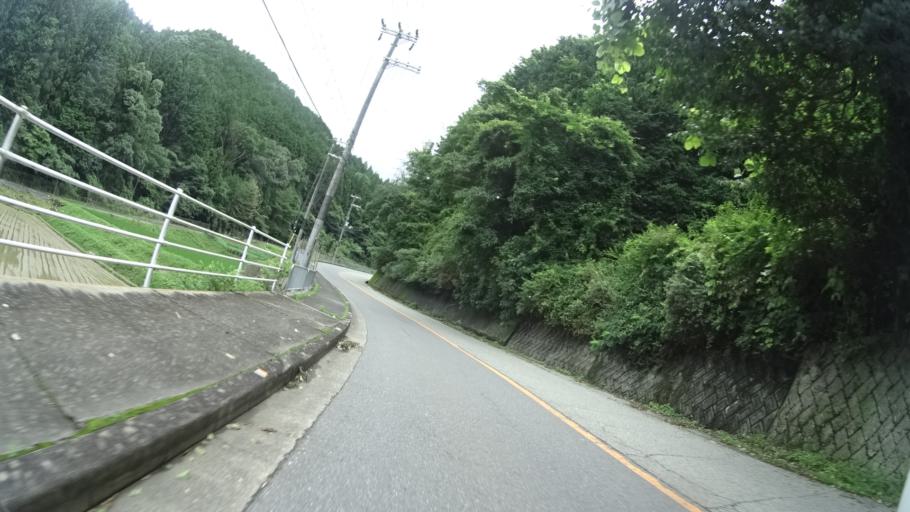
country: JP
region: Kyoto
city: Kameoka
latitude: 34.9699
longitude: 135.4826
